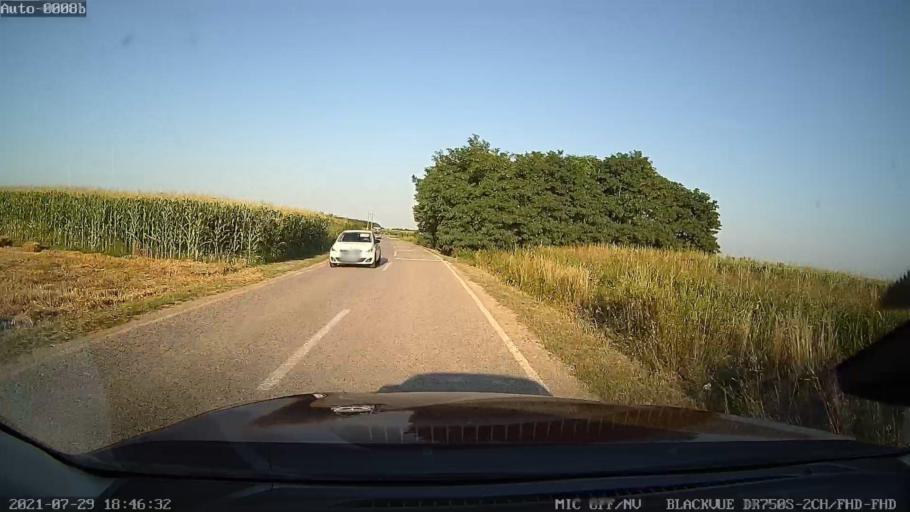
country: HR
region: Varazdinska
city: Sracinec
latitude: 46.3145
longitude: 16.2636
